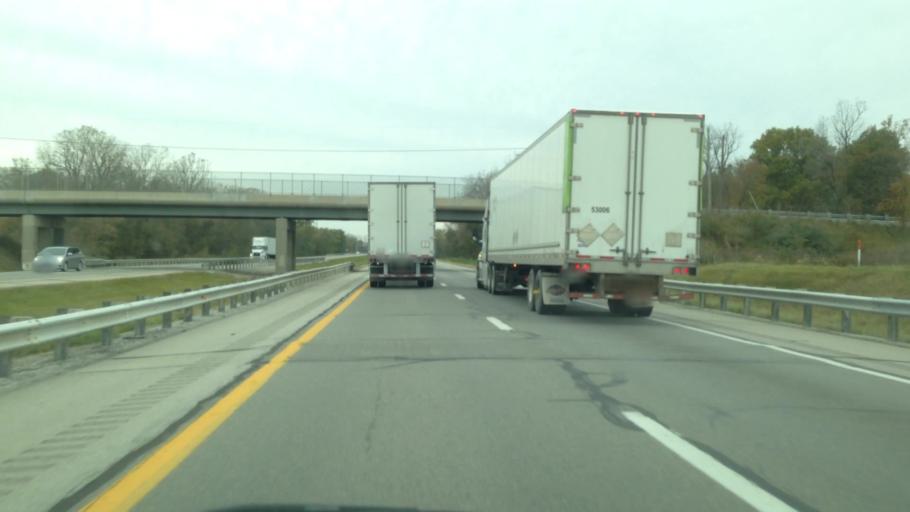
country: US
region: Ohio
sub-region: Williams County
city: Montpelier
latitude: 41.6169
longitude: -84.5828
